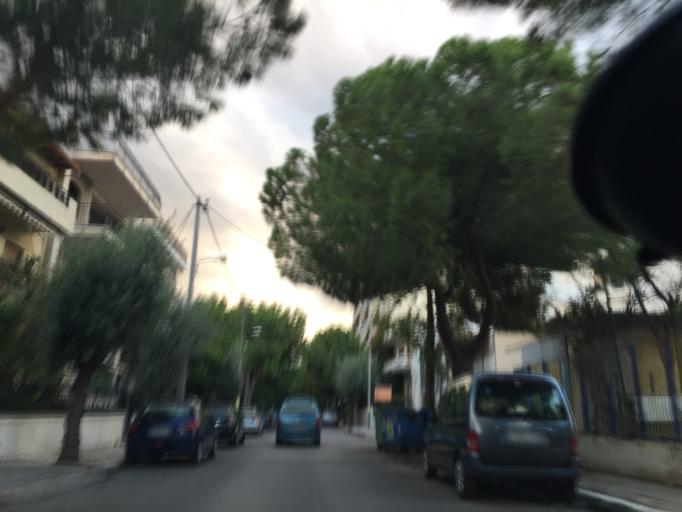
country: GR
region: Attica
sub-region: Nomarchia Athinas
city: Moskhaton
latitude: 37.9512
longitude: 23.6885
